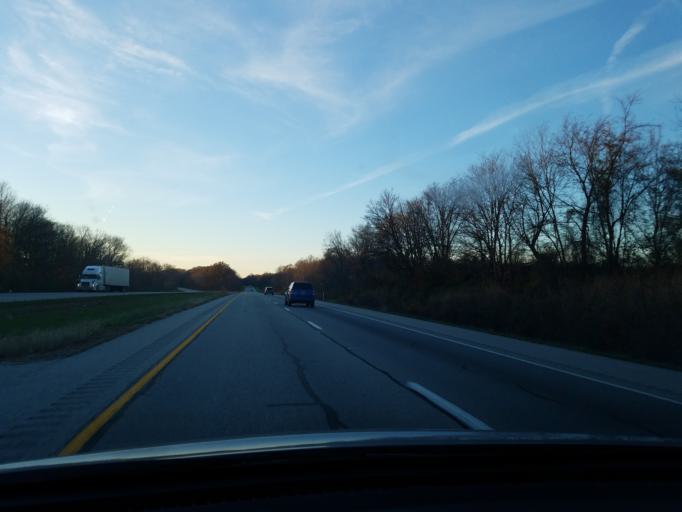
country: US
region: Indiana
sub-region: Posey County
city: Poseyville
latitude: 38.1907
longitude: -87.8344
